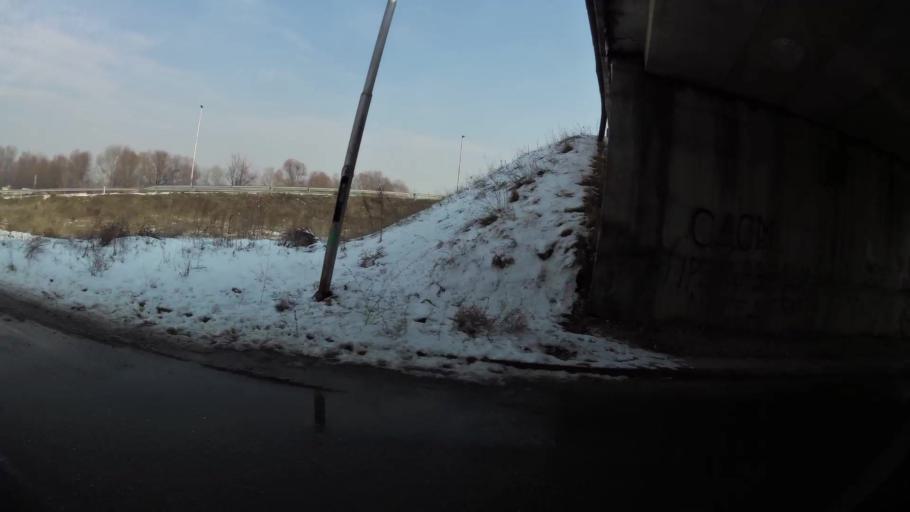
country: MK
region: Cucer-Sandevo
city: Chucher - Sandevo
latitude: 42.0534
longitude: 21.3643
